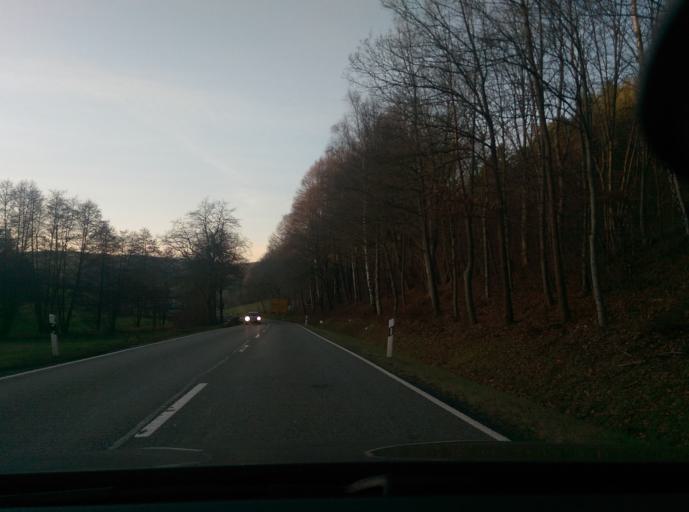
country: DE
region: Thuringia
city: Gerstungen
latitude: 51.0264
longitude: 10.0164
